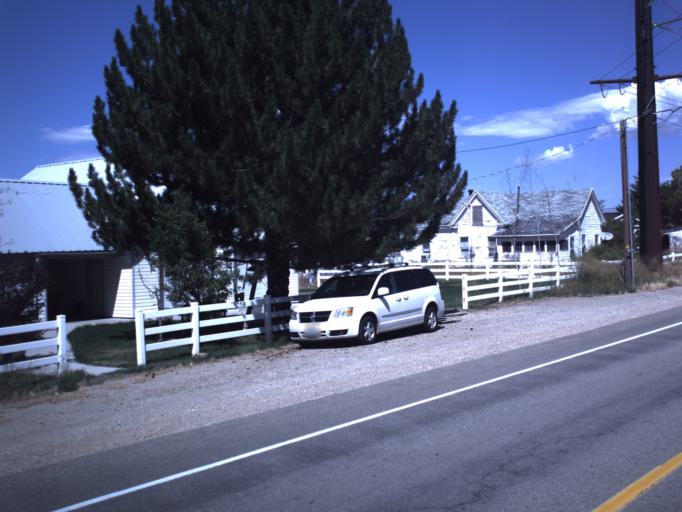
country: US
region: Utah
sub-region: Summit County
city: Kamas
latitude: 40.6682
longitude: -111.2808
